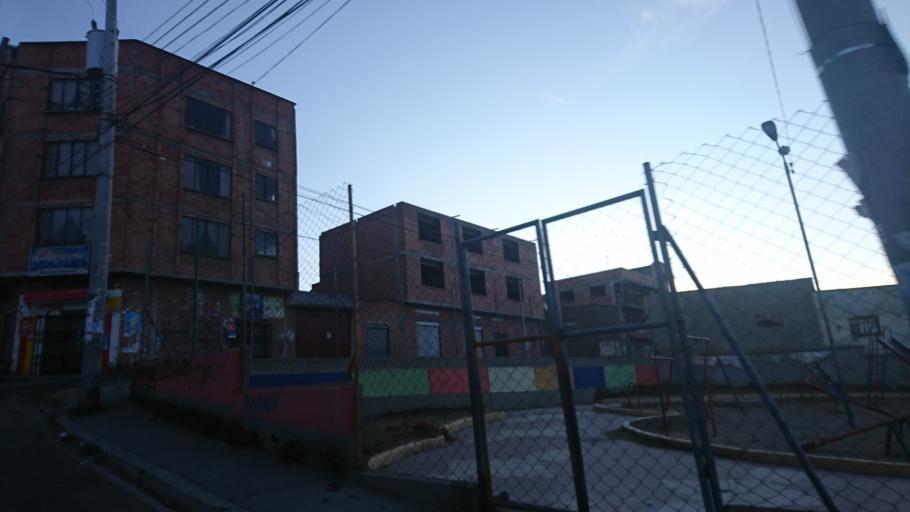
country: BO
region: La Paz
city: La Paz
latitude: -16.4906
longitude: -68.1048
